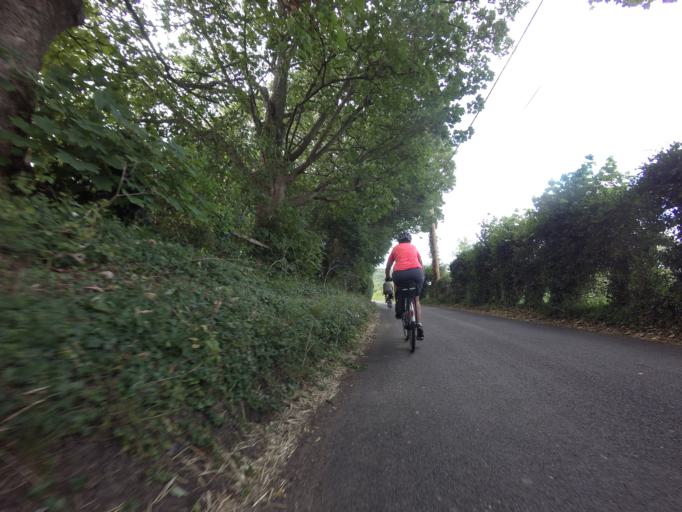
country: GB
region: England
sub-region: Kent
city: Shoreham
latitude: 51.3142
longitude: 0.1663
